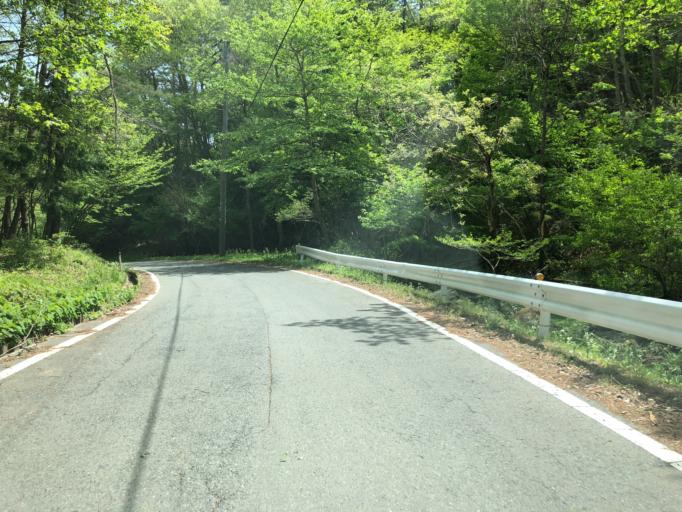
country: JP
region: Miyagi
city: Marumori
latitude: 37.6974
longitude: 140.7783
